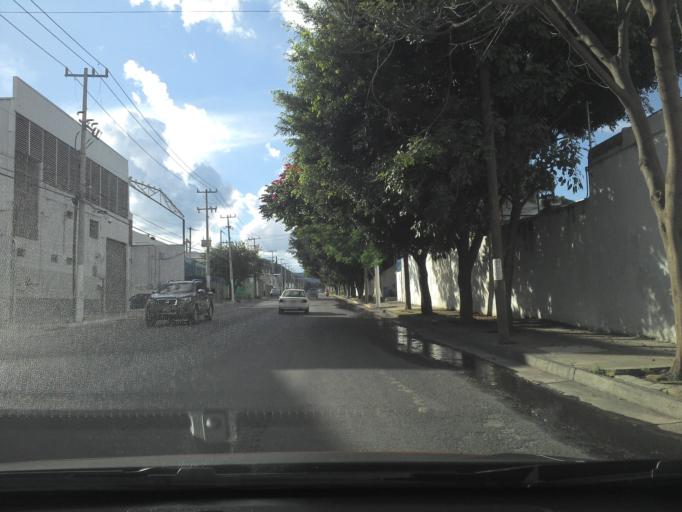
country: MX
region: Jalisco
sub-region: Tlajomulco de Zuniga
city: Palomar
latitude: 20.6165
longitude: -103.4458
